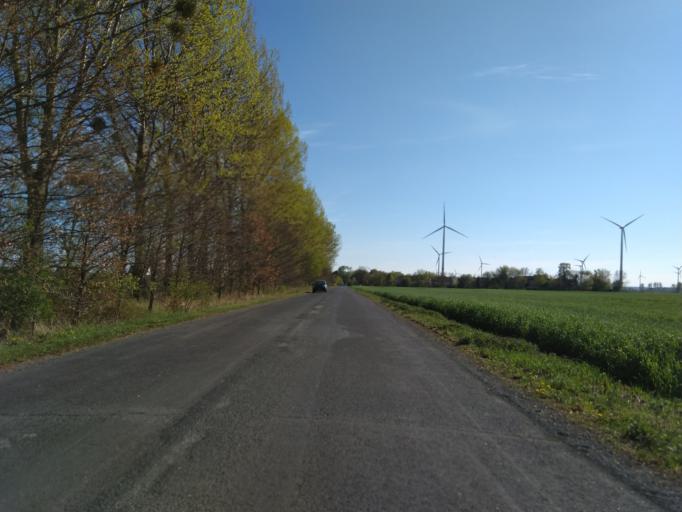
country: DE
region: Brandenburg
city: Neutrebbin
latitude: 52.7196
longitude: 14.2120
